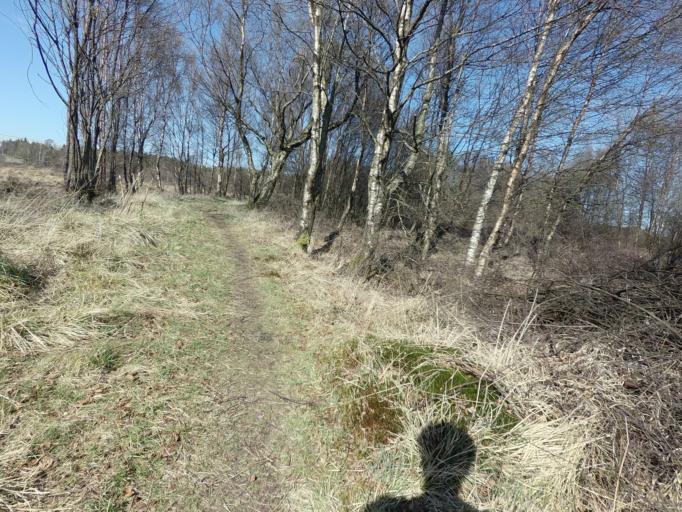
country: GB
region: Scotland
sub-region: West Lothian
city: West Calder
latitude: 55.8932
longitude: -3.5829
